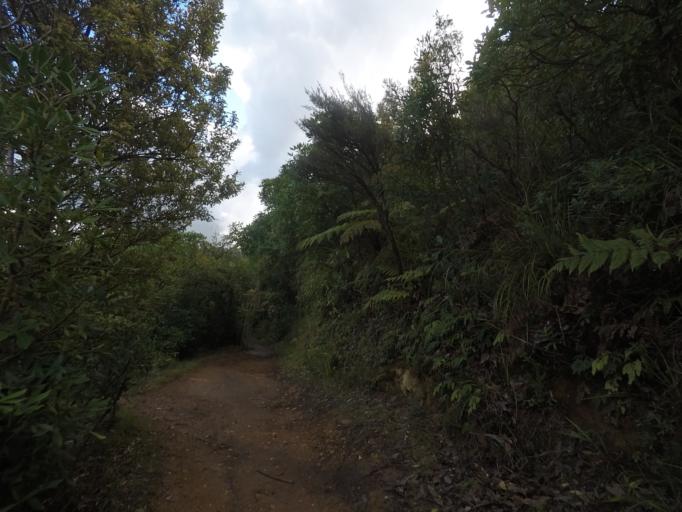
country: NZ
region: Bay of Plenty
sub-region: Western Bay of Plenty District
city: Waihi Beach
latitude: -37.3887
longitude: 175.9422
